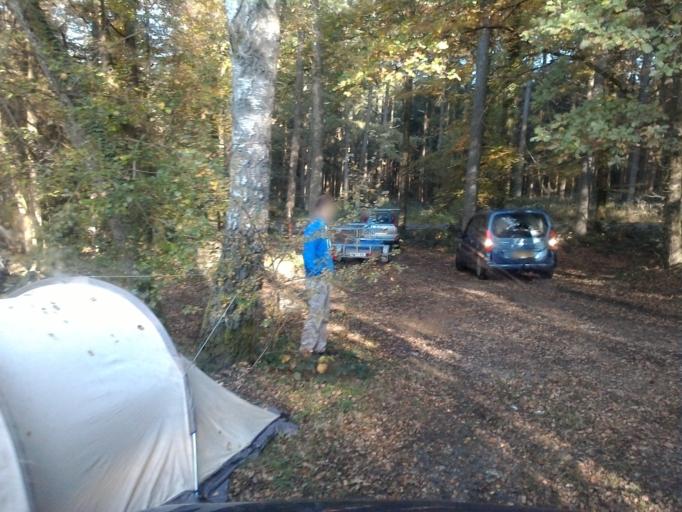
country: BE
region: Wallonia
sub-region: Province du Luxembourg
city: Chiny
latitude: 49.7399
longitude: 5.3498
